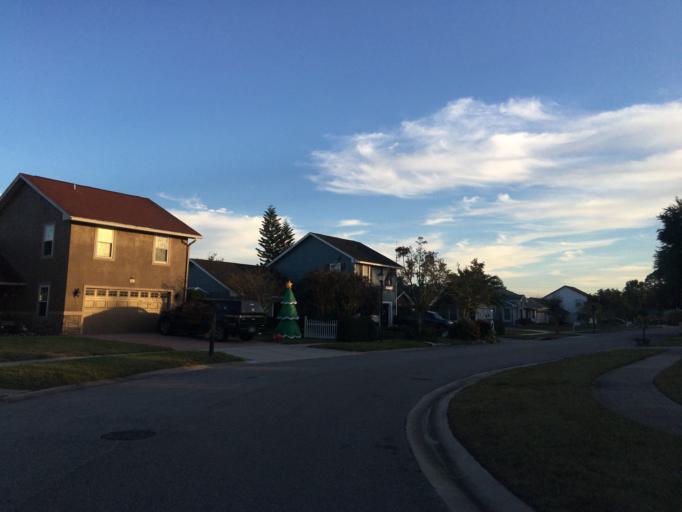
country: US
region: Florida
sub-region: Orange County
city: Azalea Park
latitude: 28.5167
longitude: -81.2754
